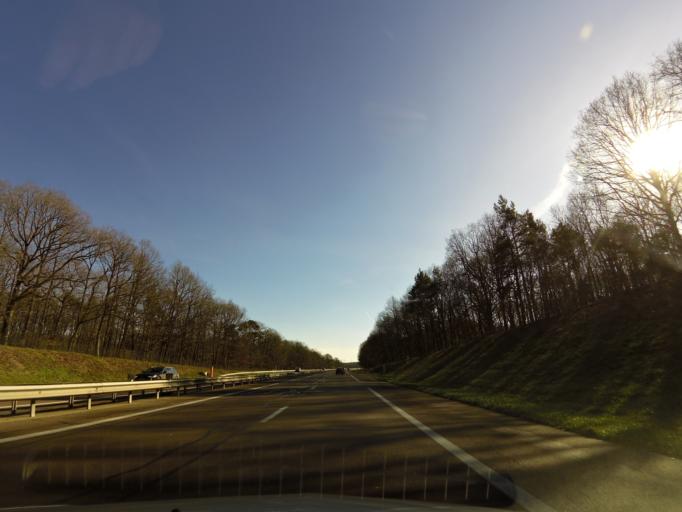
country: FR
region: Bourgogne
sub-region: Departement de l'Yonne
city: Venoy
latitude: 47.8372
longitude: 3.6175
